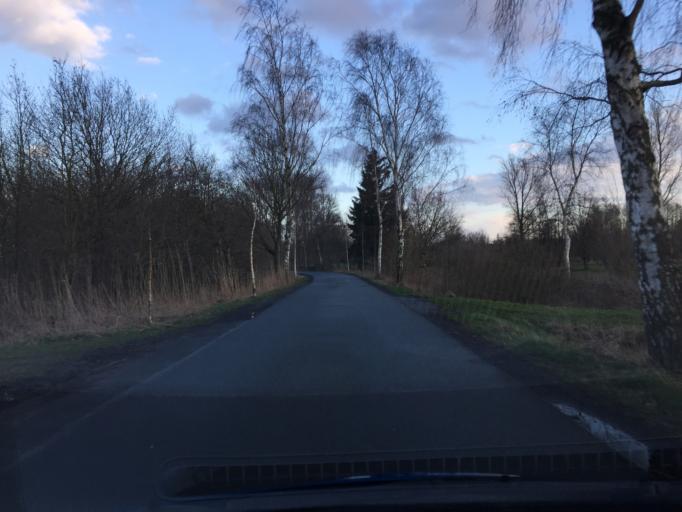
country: DE
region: Lower Saxony
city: Ludersburg
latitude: 53.3252
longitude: 10.5554
